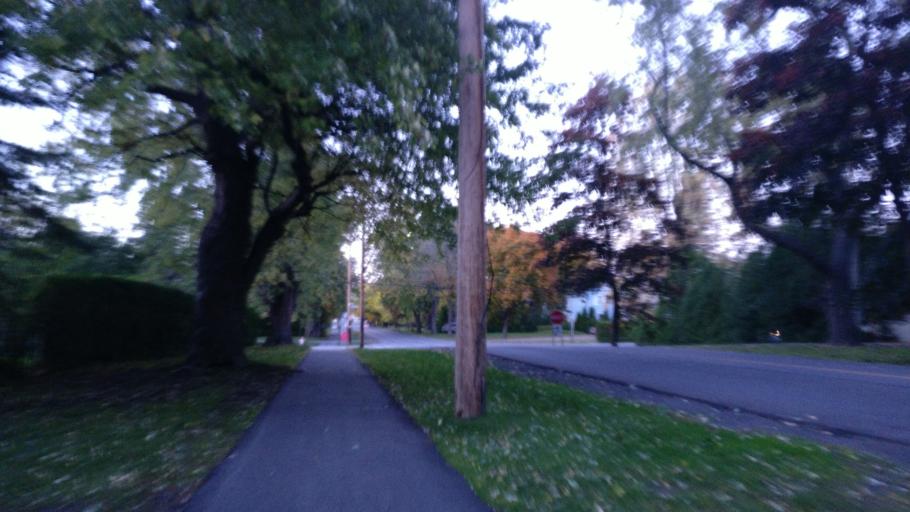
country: CA
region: Quebec
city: Baie-D'Urfe
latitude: 45.4142
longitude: -73.9163
